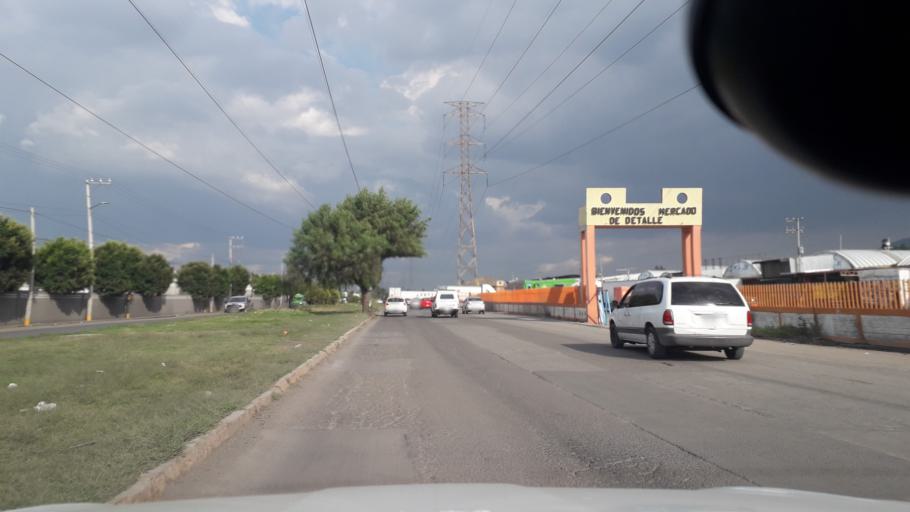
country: MX
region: Mexico
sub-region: Tultitlan
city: Fuentes del Valle
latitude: 19.6398
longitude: -99.1450
